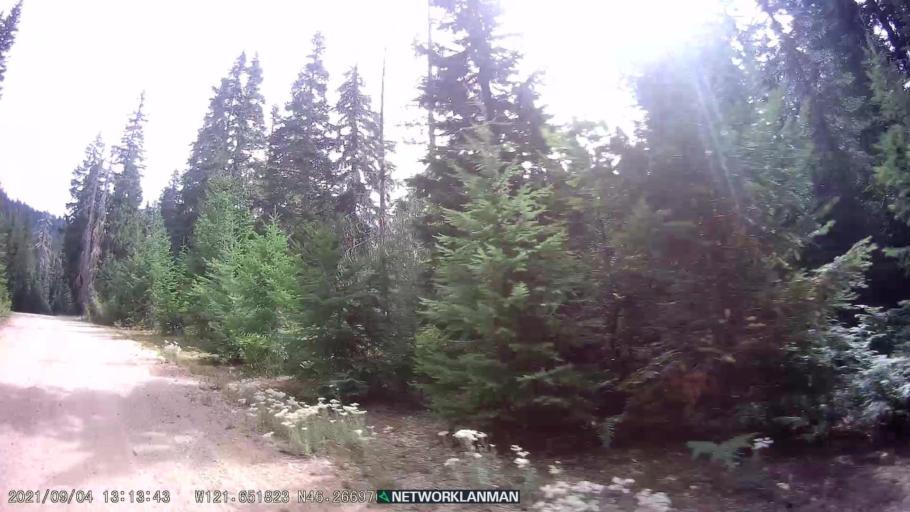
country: US
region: Washington
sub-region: Klickitat County
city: White Salmon
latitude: 46.2670
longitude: -121.6518
